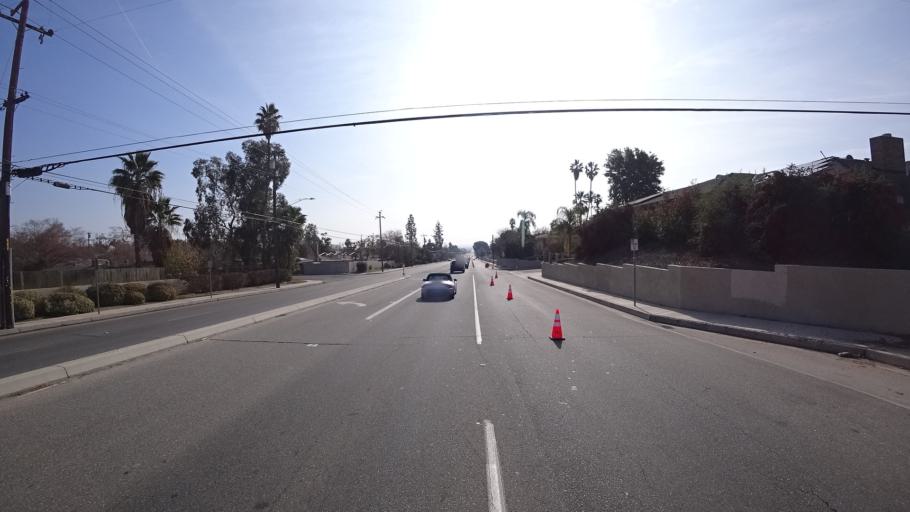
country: US
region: California
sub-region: Kern County
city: Bakersfield
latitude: 35.3887
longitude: -118.9498
